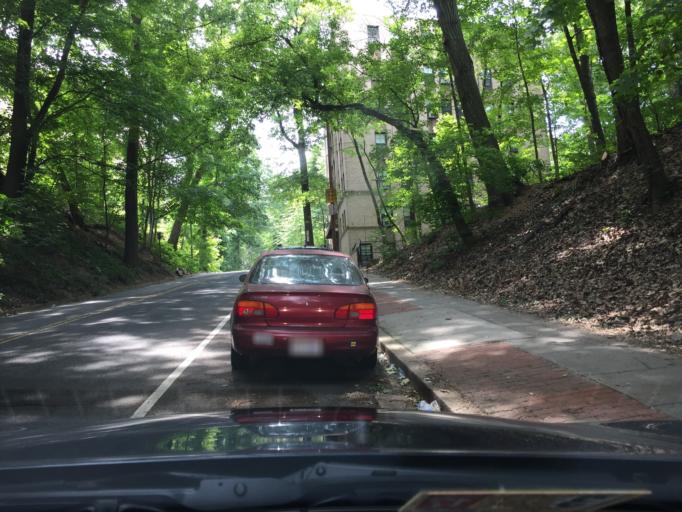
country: US
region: Washington, D.C.
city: Washington, D.C.
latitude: 38.9272
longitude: -77.0430
